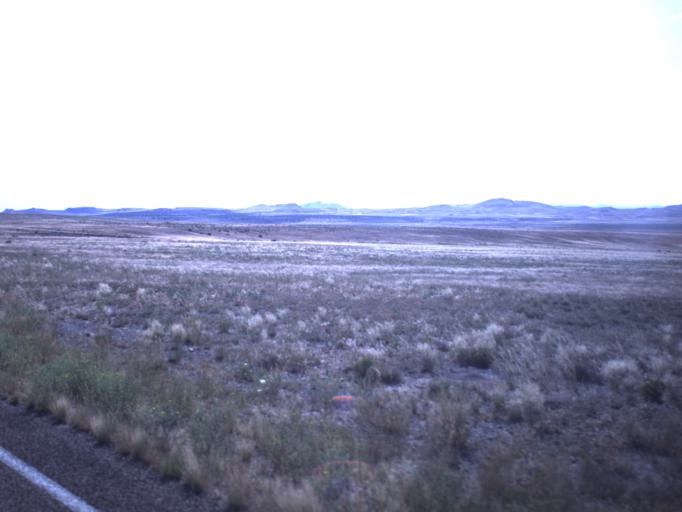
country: US
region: Utah
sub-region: Beaver County
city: Milford
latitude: 38.7929
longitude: -112.9060
